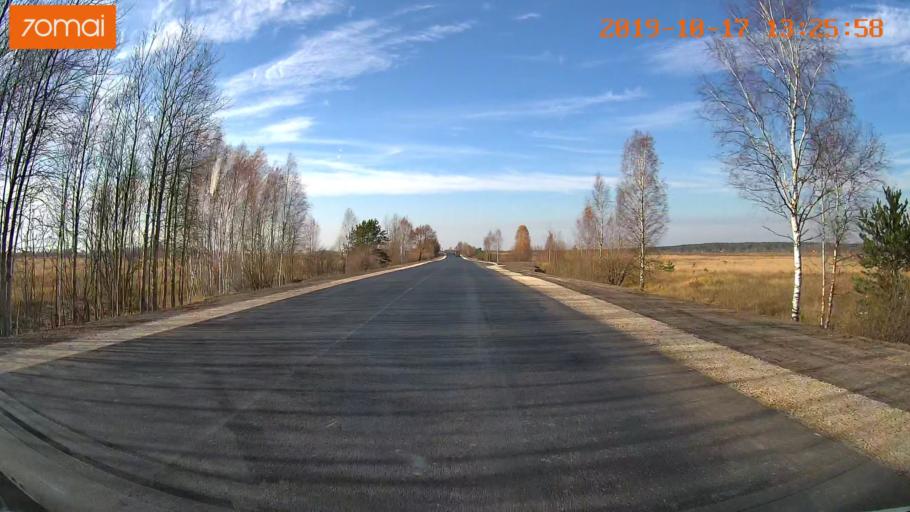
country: RU
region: Rjazan
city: Gus'-Zheleznyy
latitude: 55.1067
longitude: 40.9323
